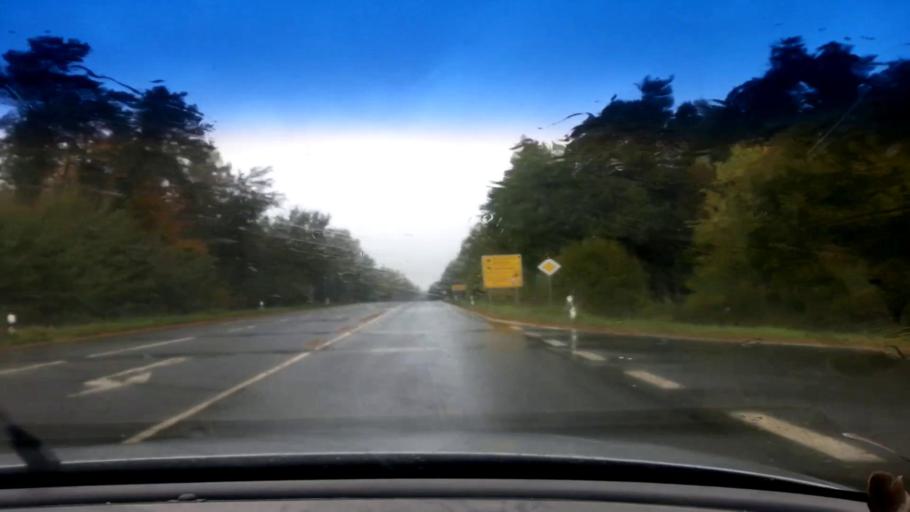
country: DE
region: Bavaria
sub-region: Upper Franconia
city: Stadelhofen
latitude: 50.0009
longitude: 11.2071
